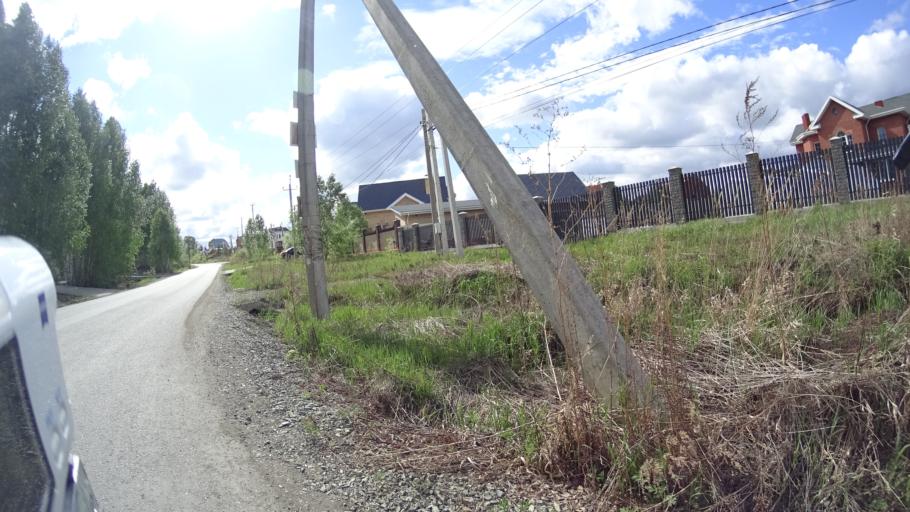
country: RU
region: Chelyabinsk
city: Sargazy
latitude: 55.1520
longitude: 61.2398
